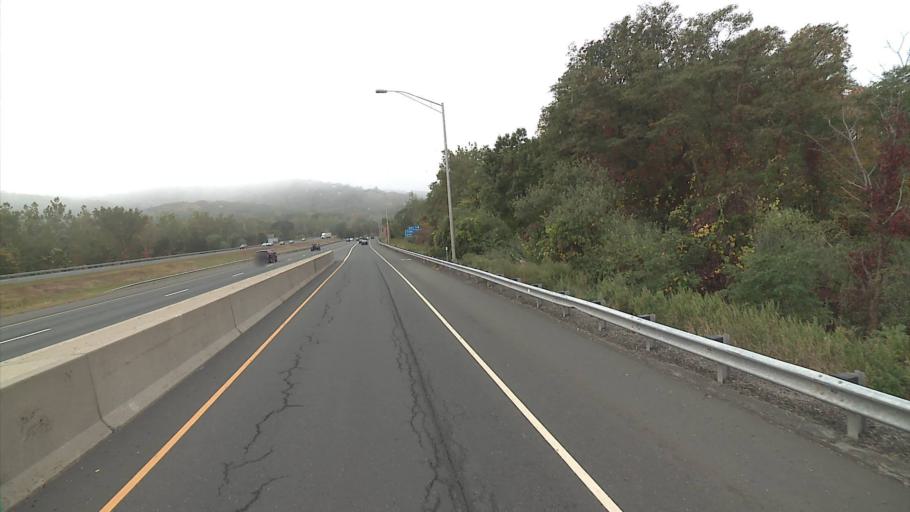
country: US
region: Connecticut
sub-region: New Haven County
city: Southbury
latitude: 41.4694
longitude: -73.2199
